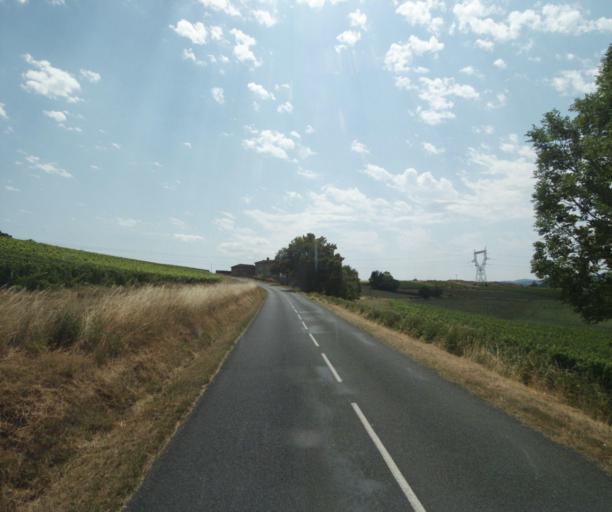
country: FR
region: Rhone-Alpes
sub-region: Departement du Rhone
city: Chatillon
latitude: 45.8717
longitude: 4.6038
